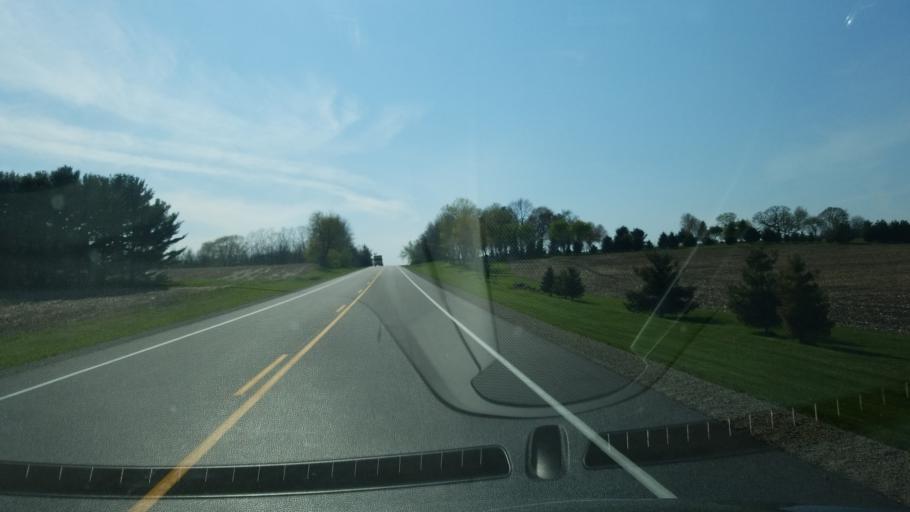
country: US
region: Wisconsin
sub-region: Dane County
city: Fitchburg
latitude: 42.9505
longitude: -89.4480
